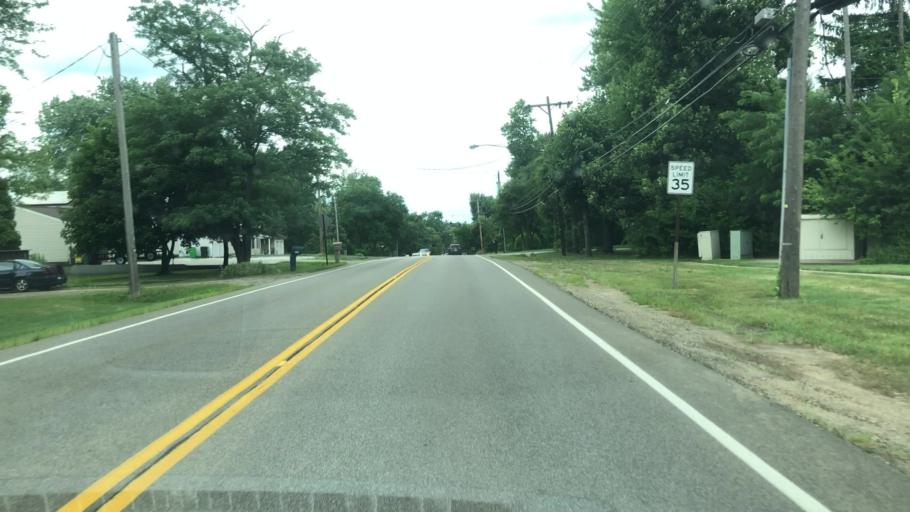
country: US
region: Ohio
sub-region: Summit County
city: Stow
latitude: 41.1768
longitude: -81.4148
